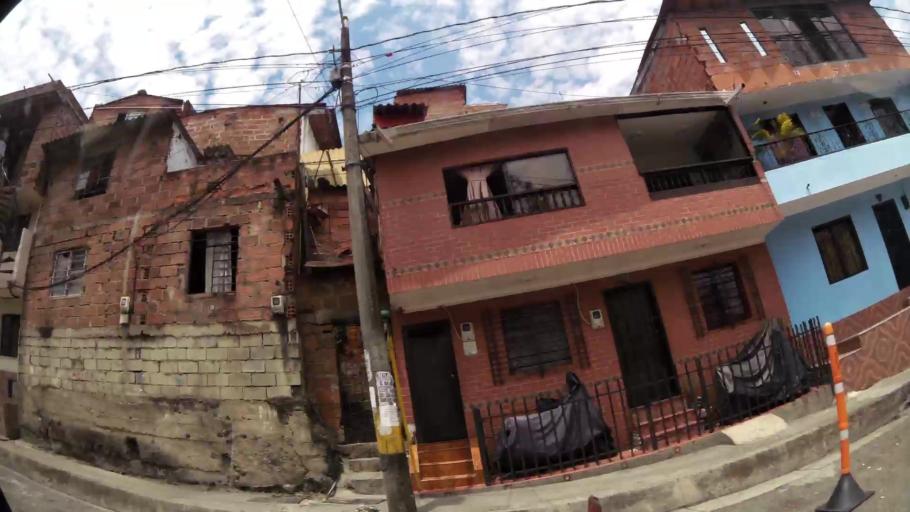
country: CO
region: Antioquia
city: Bello
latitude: 6.3096
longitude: -75.5790
